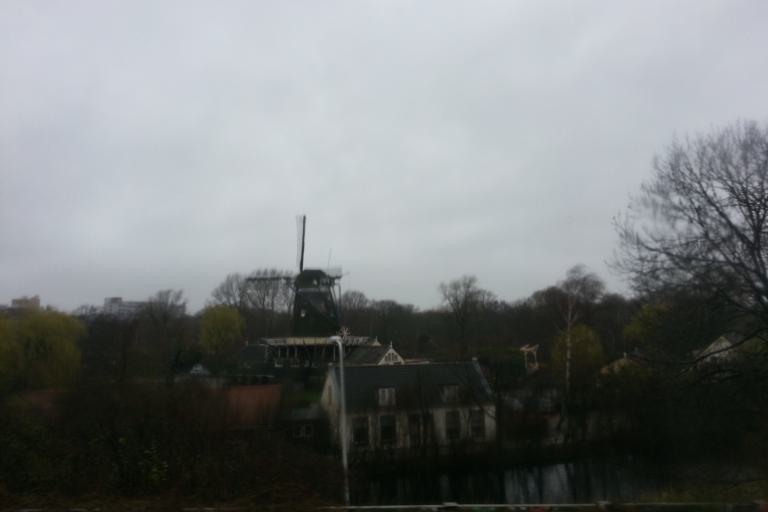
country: NL
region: South Holland
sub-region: Gemeente Leiden
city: Leiden
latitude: 52.1729
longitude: 4.4905
